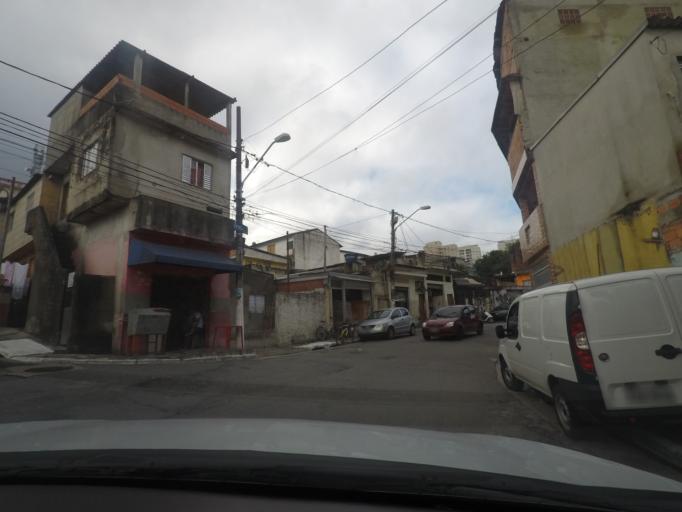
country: BR
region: Sao Paulo
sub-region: Diadema
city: Diadema
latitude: -23.6579
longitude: -46.6624
